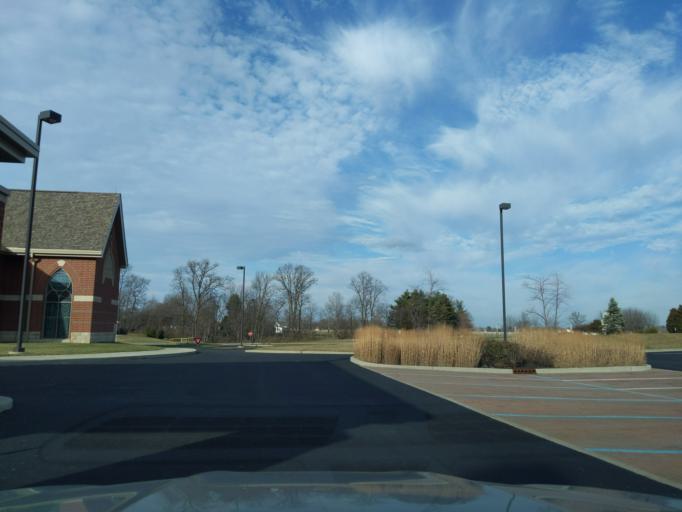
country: US
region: Indiana
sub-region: Decatur County
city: Greensburg
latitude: 39.3204
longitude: -85.4651
